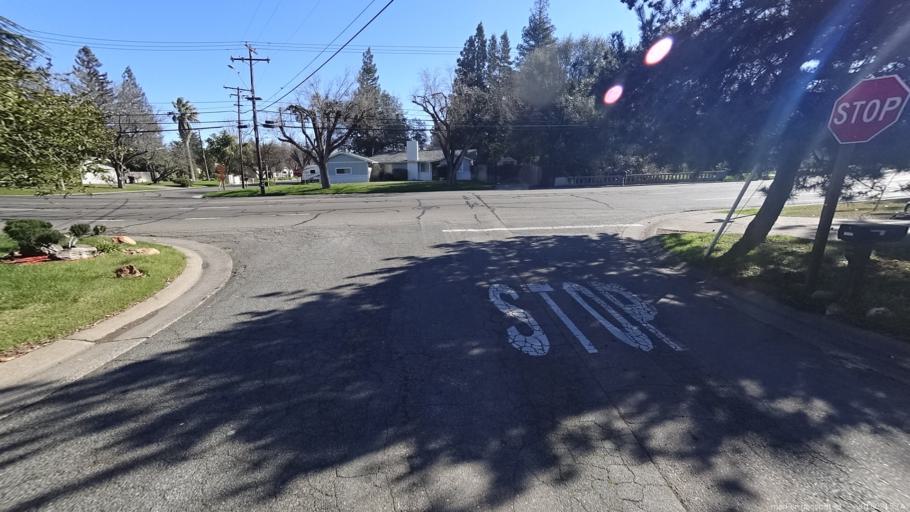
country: US
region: California
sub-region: Sacramento County
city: Foothill Farms
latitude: 38.6690
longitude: -121.3089
